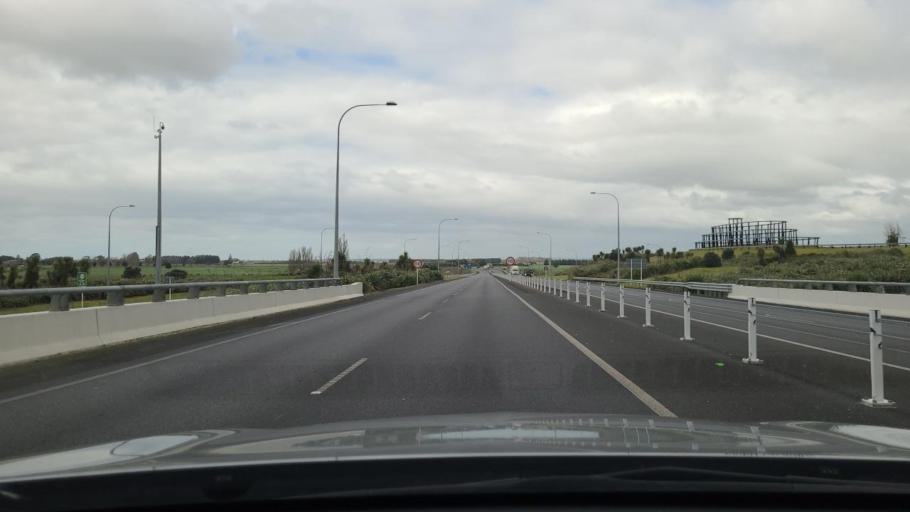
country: NZ
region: Bay of Plenty
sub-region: Tauranga City
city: Tauranga
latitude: -37.7156
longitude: 176.2849
